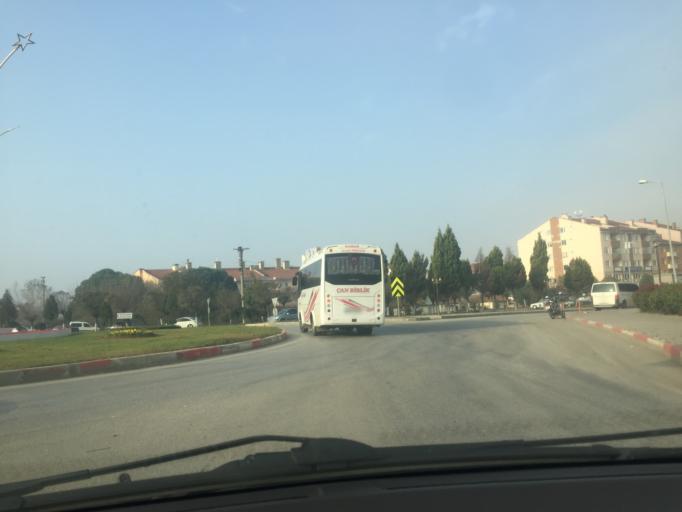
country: TR
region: Canakkale
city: Can
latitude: 40.0252
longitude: 27.0500
